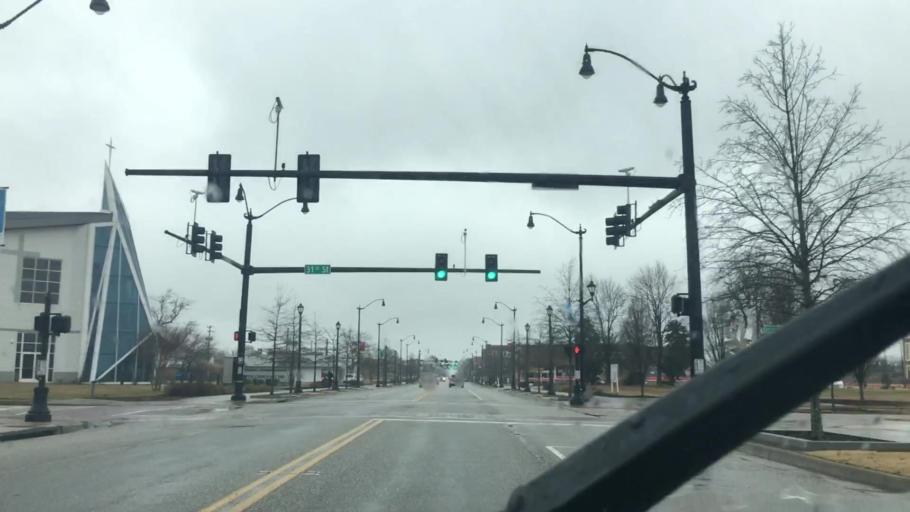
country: US
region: Virginia
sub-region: City of Newport News
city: Newport News
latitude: 36.9855
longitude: -76.4236
